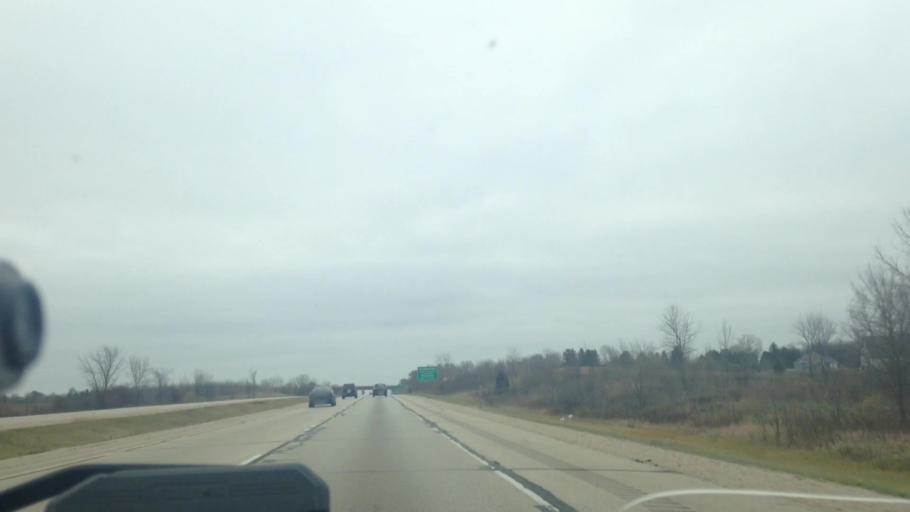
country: US
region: Wisconsin
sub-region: Washington County
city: Richfield
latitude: 43.2999
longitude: -88.2174
